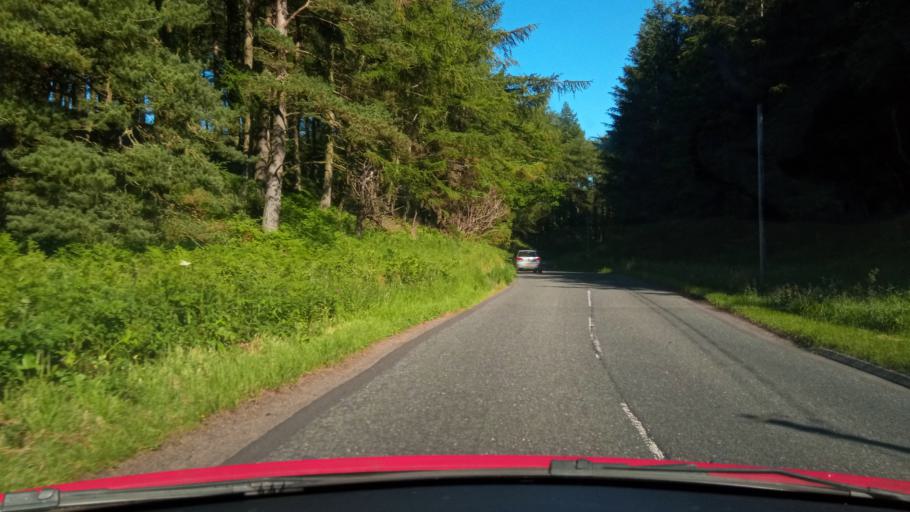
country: GB
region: Scotland
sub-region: The Scottish Borders
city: Duns
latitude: 55.8281
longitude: -2.3280
